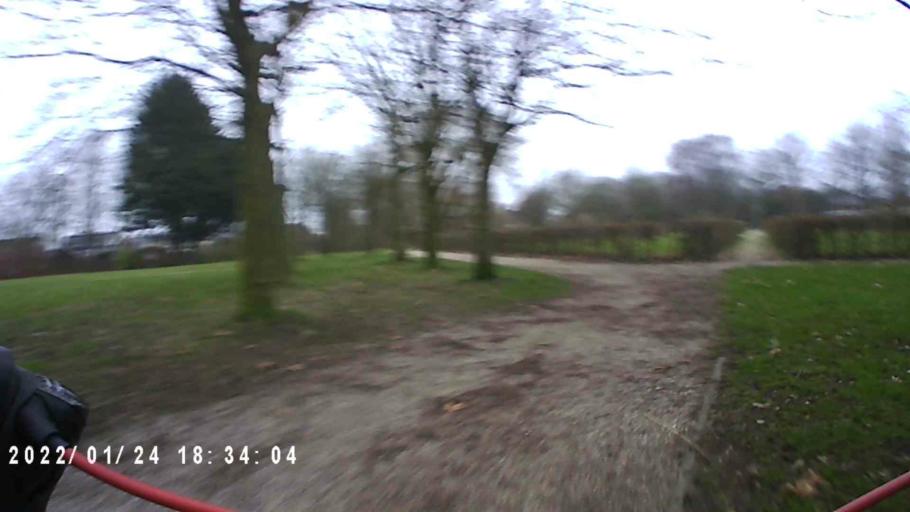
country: NL
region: Groningen
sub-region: Gemeente De Marne
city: Ulrum
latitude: 53.3563
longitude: 6.3362
